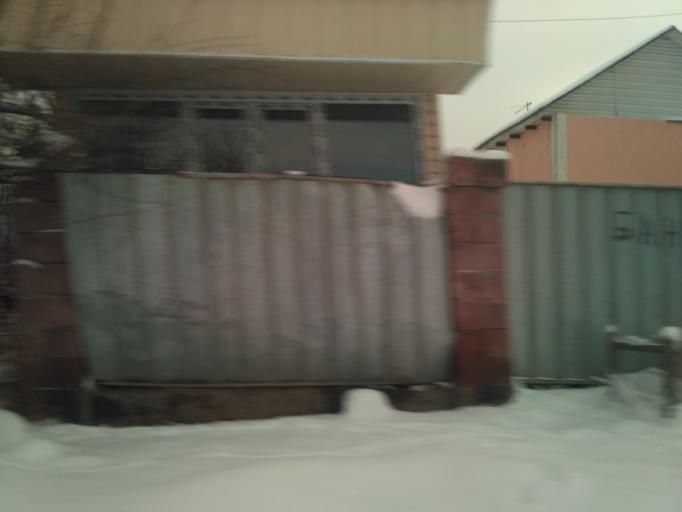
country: KZ
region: Almaty Qalasy
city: Almaty
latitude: 43.2121
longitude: 76.7776
